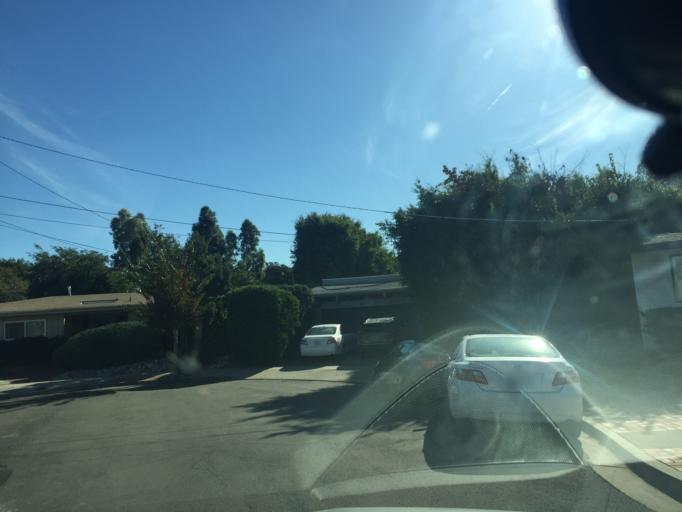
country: US
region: California
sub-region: San Diego County
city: Lemon Grove
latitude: 32.7683
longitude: -117.0820
